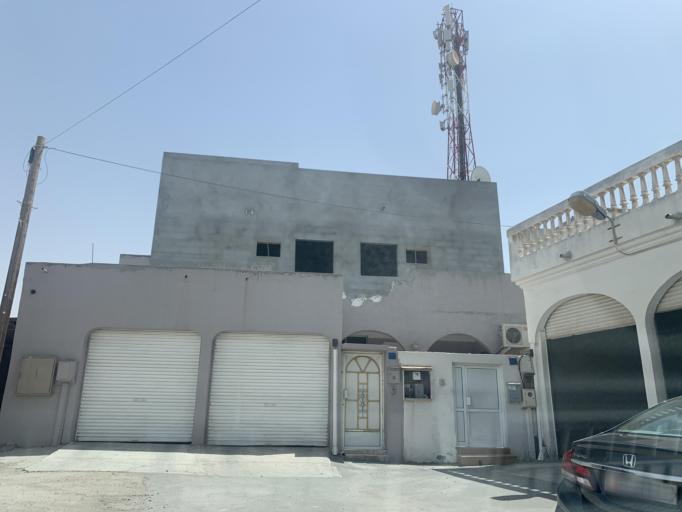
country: BH
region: Central Governorate
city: Madinat Hamad
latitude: 26.1466
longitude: 50.4990
